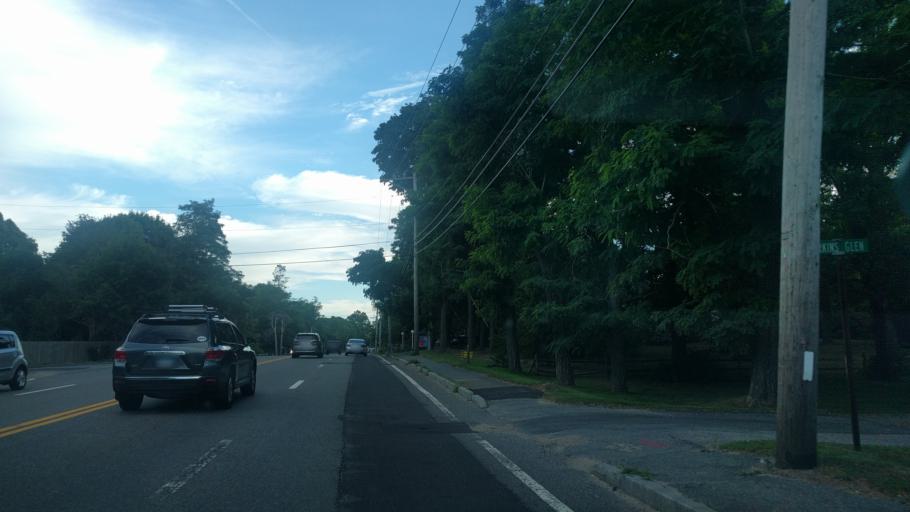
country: US
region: Massachusetts
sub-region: Barnstable County
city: Eastham
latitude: 41.8083
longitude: -69.9737
